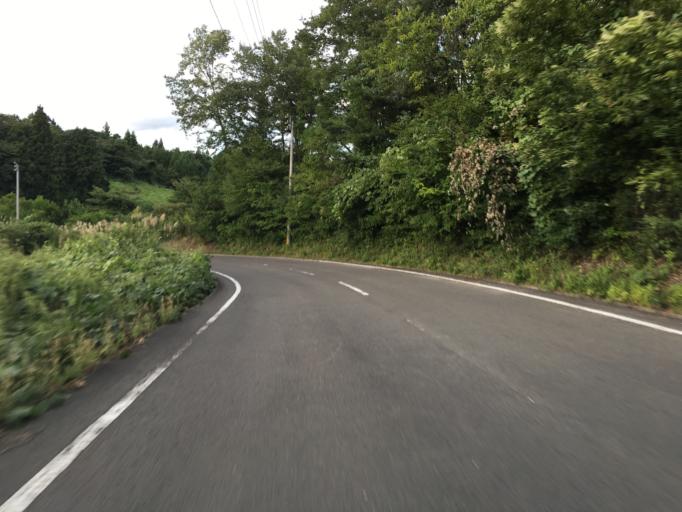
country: JP
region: Fukushima
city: Nihommatsu
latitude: 37.6243
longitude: 140.4983
